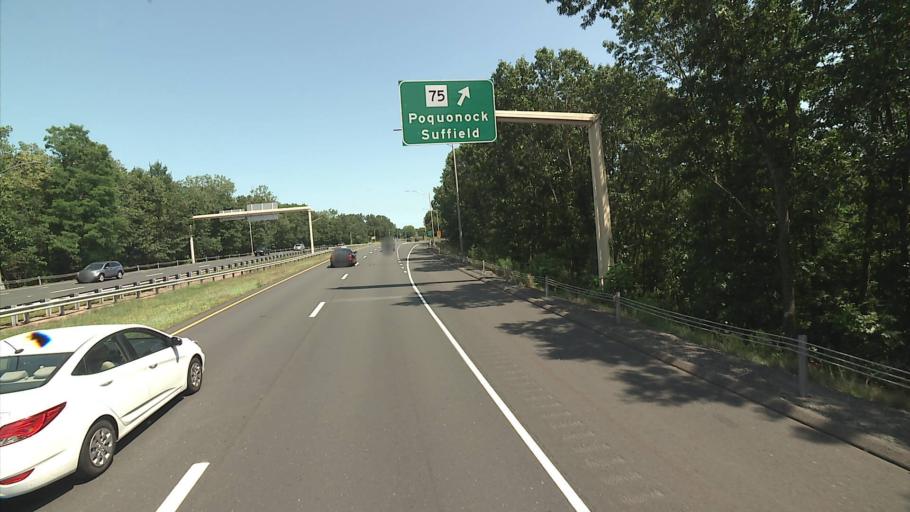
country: US
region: Connecticut
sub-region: Hartford County
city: Windsor Locks
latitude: 41.9174
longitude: -72.6802
